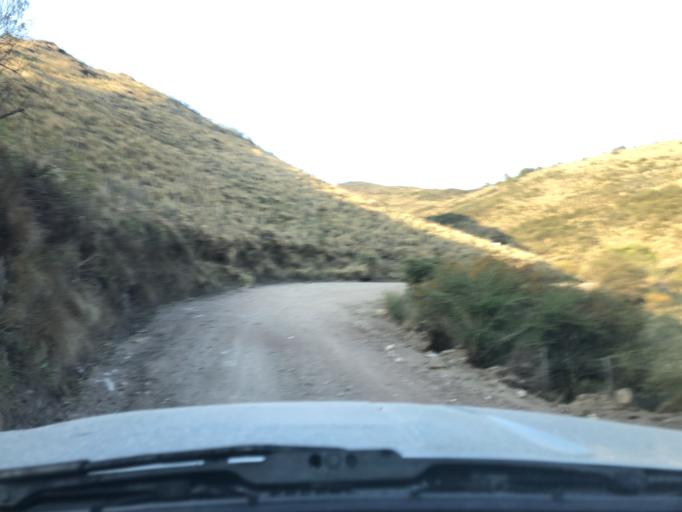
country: AR
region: Cordoba
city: Agua de Oro
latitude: -31.0554
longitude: -64.3546
